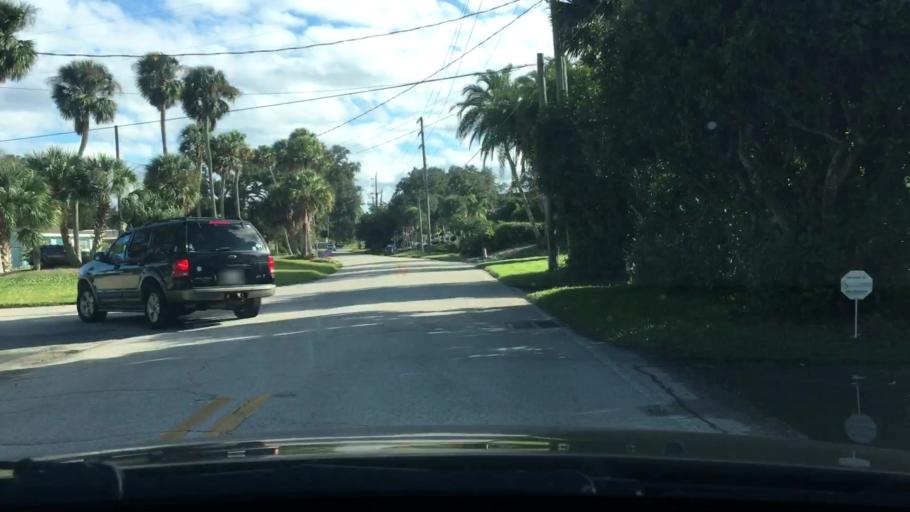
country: US
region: Florida
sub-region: Volusia County
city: Ormond-by-the-Sea
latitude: 29.3206
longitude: -81.0622
